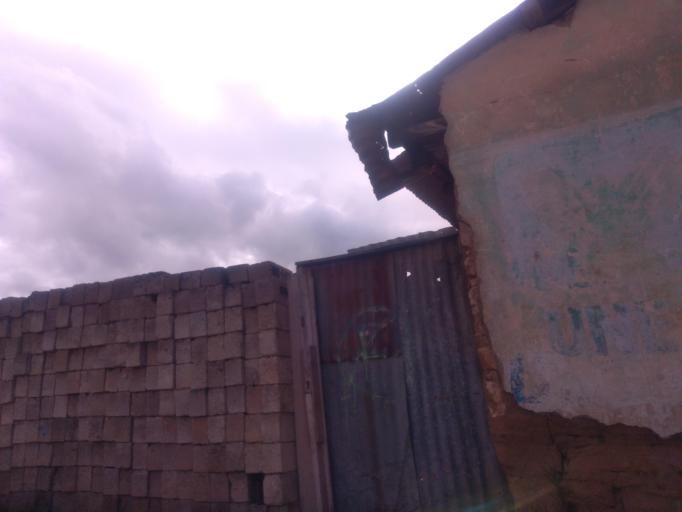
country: GT
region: Quetzaltenango
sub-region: Municipio de La Esperanza
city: La Esperanza
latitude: 14.8538
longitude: -91.5659
